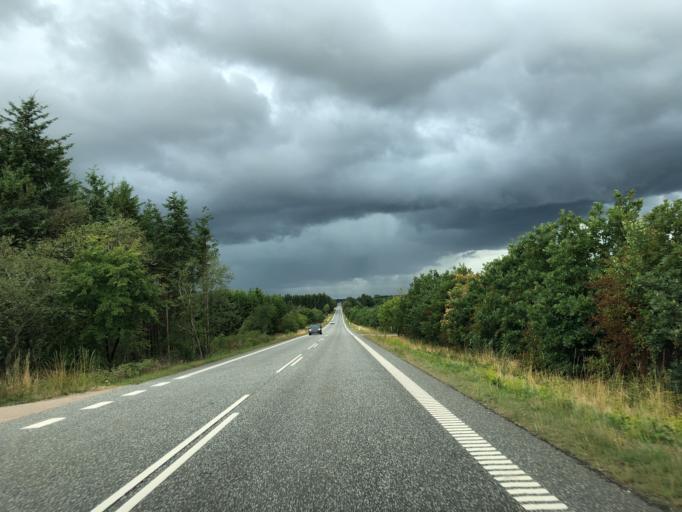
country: DK
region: Central Jutland
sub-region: Ikast-Brande Kommune
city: Bording Kirkeby
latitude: 56.1379
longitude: 9.3814
